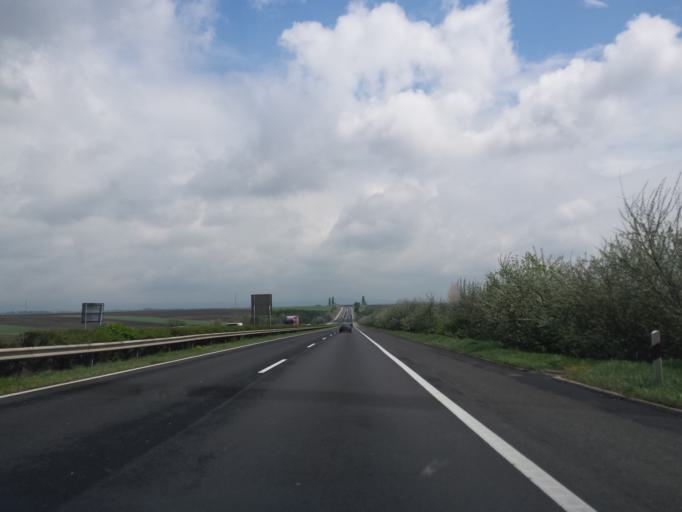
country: HU
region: Fejer
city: Many
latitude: 47.5101
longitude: 18.6603
